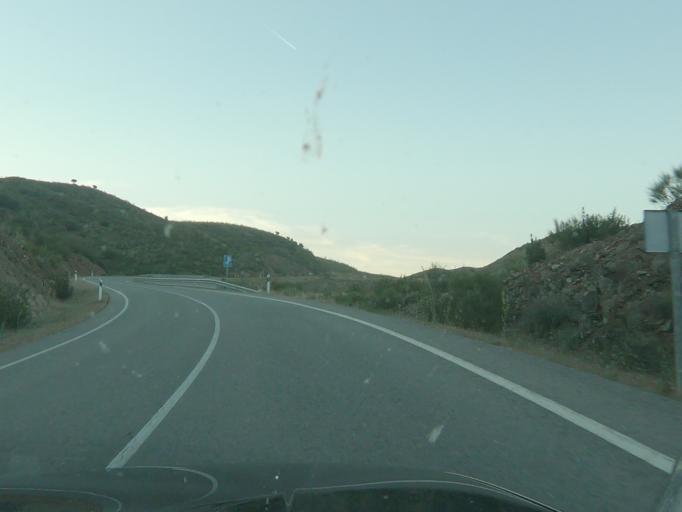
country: ES
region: Extremadura
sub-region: Provincia de Caceres
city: Salorino
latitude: 39.5787
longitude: -6.9968
